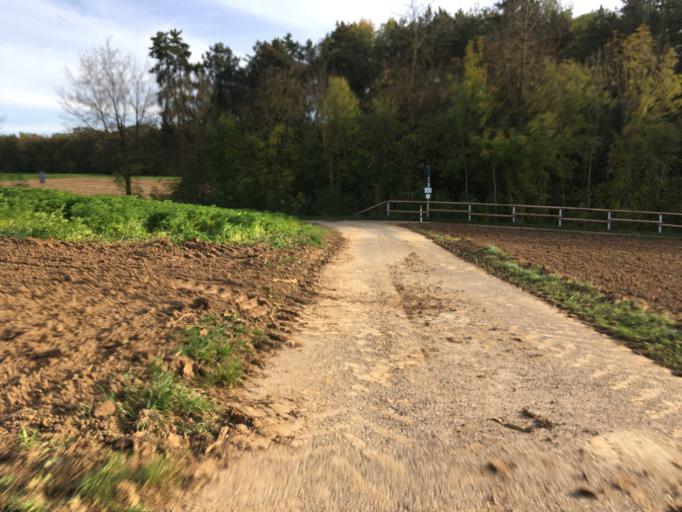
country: DE
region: Baden-Wuerttemberg
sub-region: Karlsruhe Region
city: Balzfeld
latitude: 49.2653
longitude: 8.8123
